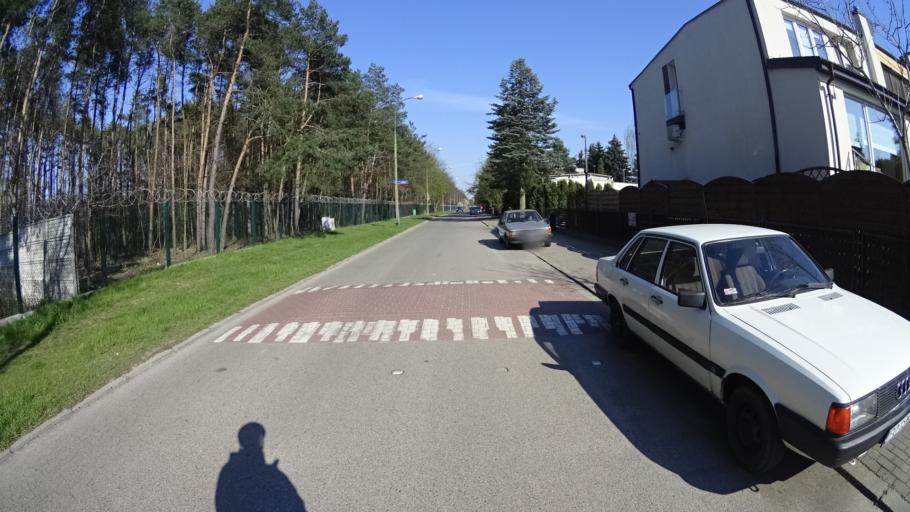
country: PL
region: Masovian Voivodeship
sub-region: Powiat warszawski zachodni
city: Babice
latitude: 52.2529
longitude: 20.8731
